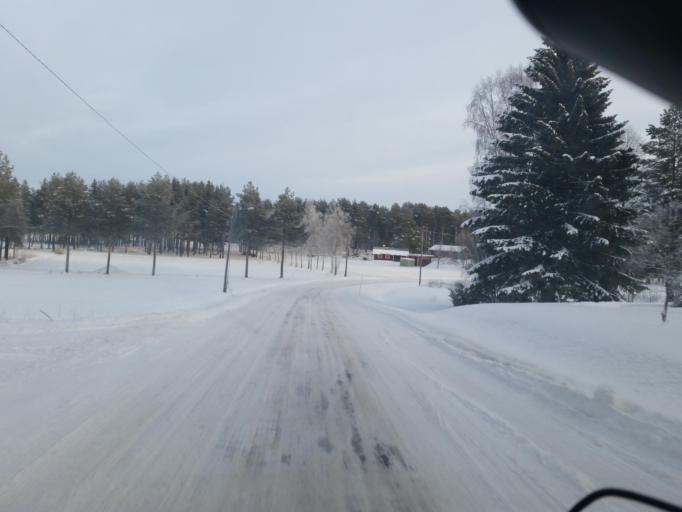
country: SE
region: Norrbotten
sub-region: Pitea Kommun
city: Rosvik
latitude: 65.3931
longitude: 21.7400
